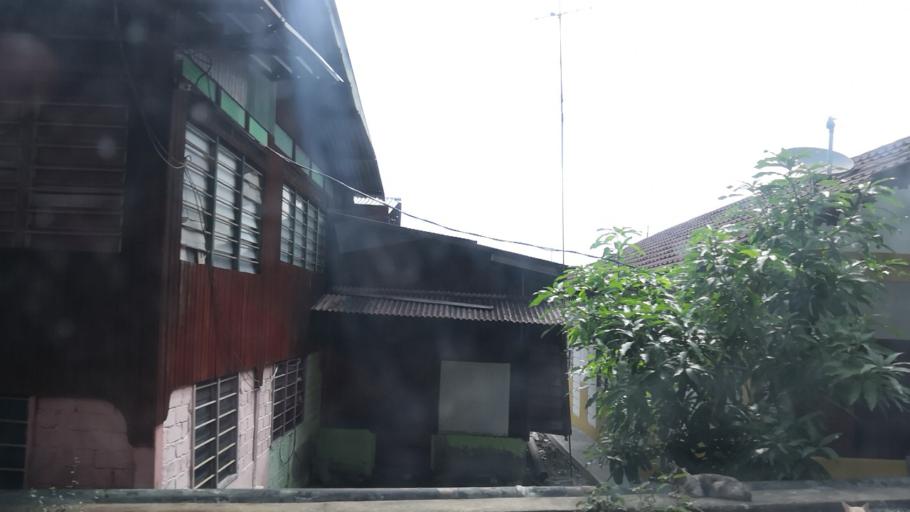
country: MY
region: Perak
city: Lumut
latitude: 4.1962
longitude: 100.5773
